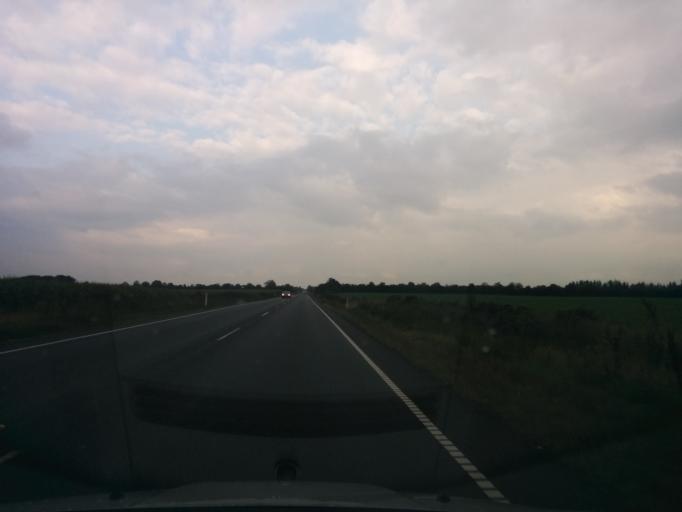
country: DK
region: South Denmark
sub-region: Esbjerg Kommune
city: Bramming
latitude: 55.5869
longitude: 8.7024
